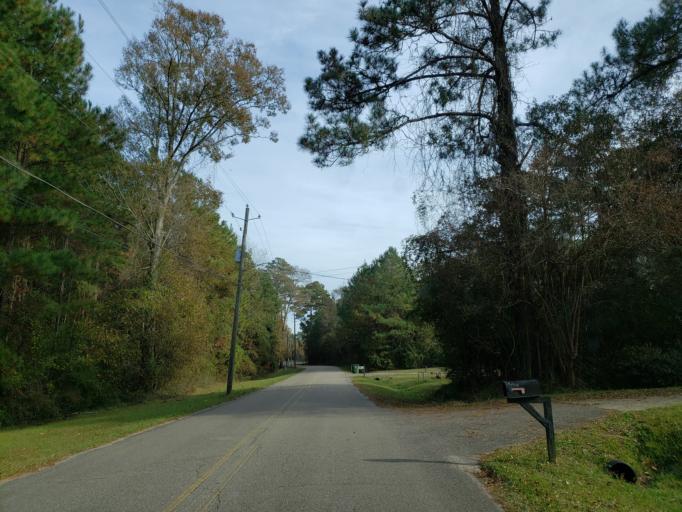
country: US
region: Mississippi
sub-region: Forrest County
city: Glendale
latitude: 31.3544
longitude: -89.3343
